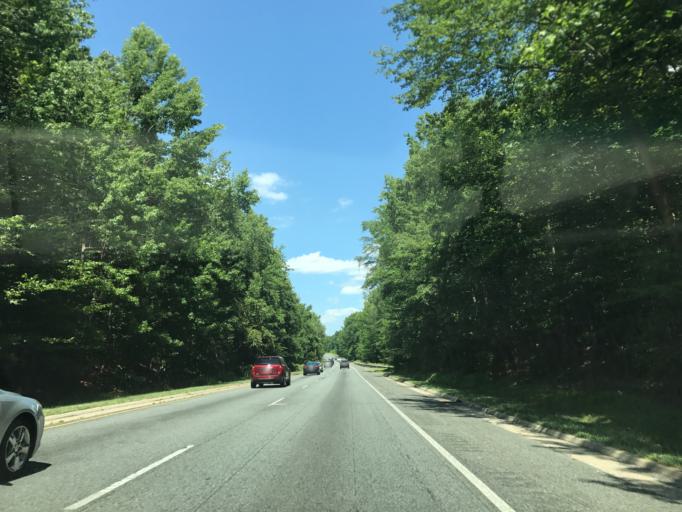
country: US
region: Maryland
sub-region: Anne Arundel County
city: Maryland City
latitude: 39.0832
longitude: -76.8164
